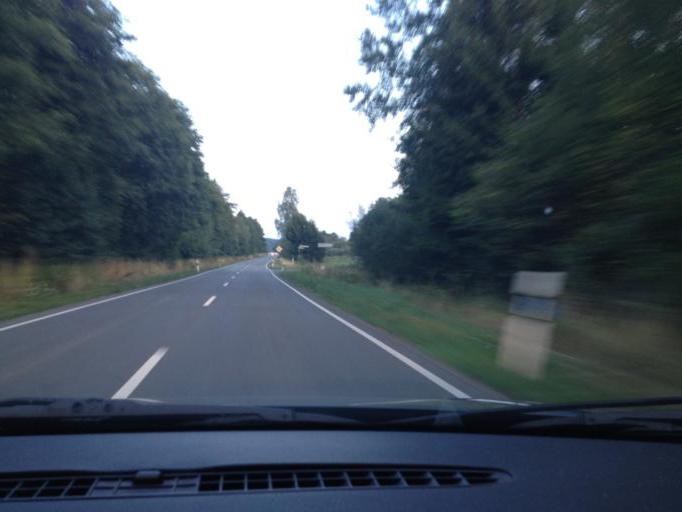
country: DE
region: Saarland
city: Nohfelden
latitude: 49.5746
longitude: 7.1131
